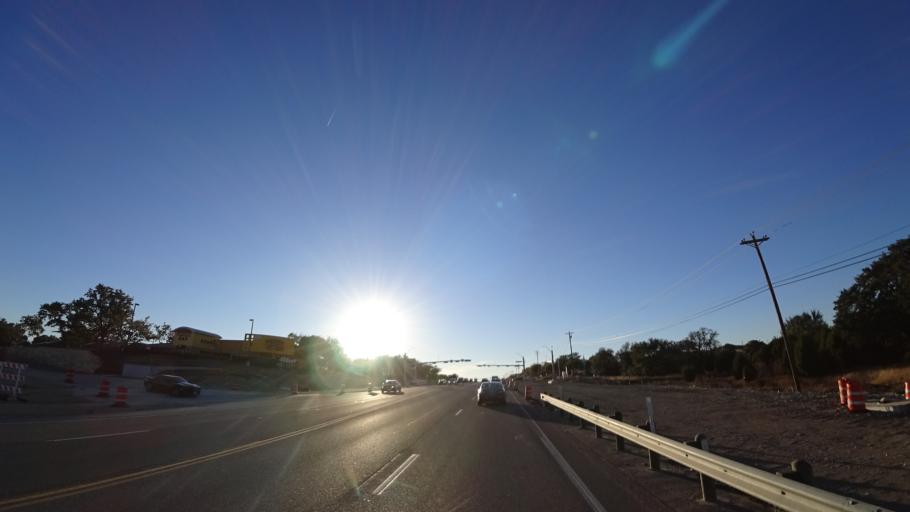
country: US
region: Texas
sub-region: Williamson County
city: Cedar Park
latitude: 30.5299
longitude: -97.7994
